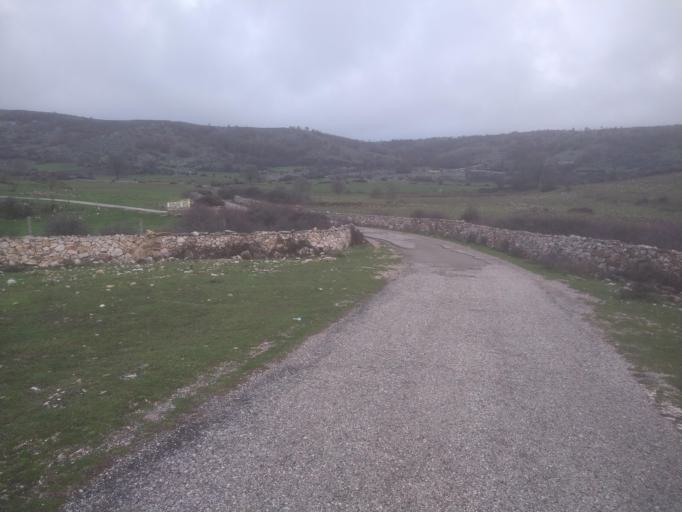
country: IT
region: Apulia
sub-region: Provincia di Foggia
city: San Giovanni Rotondo
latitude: 41.7320
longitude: 15.7507
